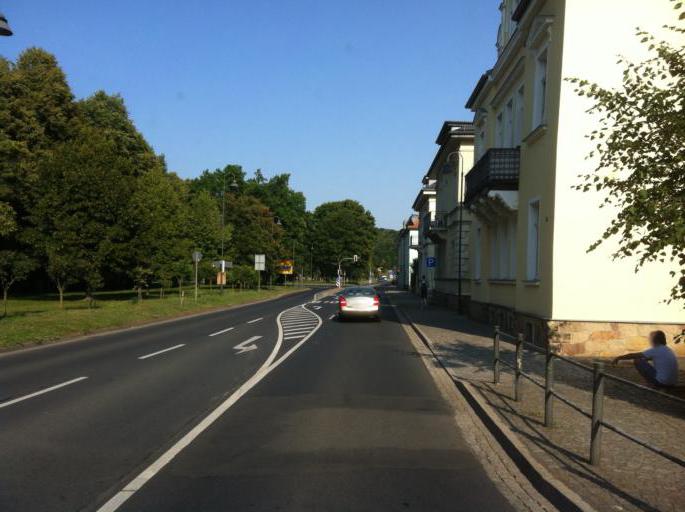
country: DE
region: Saxony
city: Grimma
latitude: 51.2387
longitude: 12.7268
